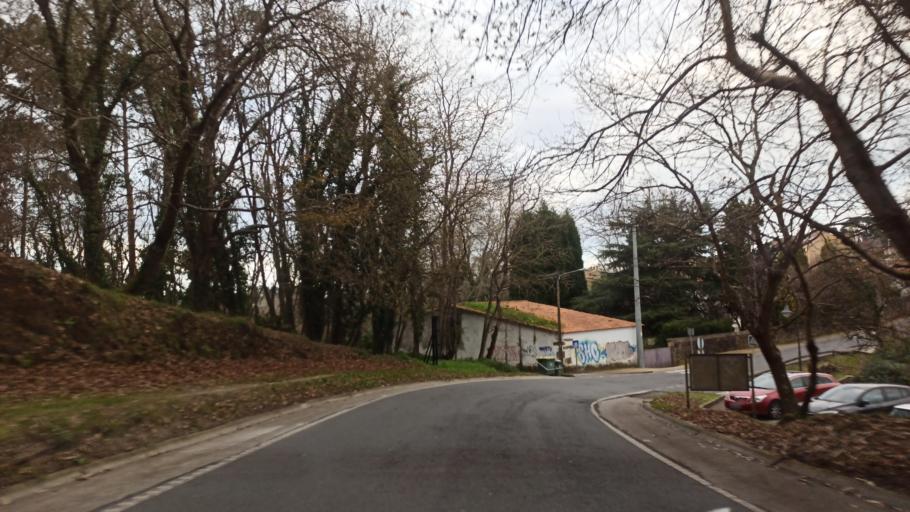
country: ES
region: Galicia
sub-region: Provincia da Coruna
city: Oleiros
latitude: 43.3351
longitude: -8.3522
